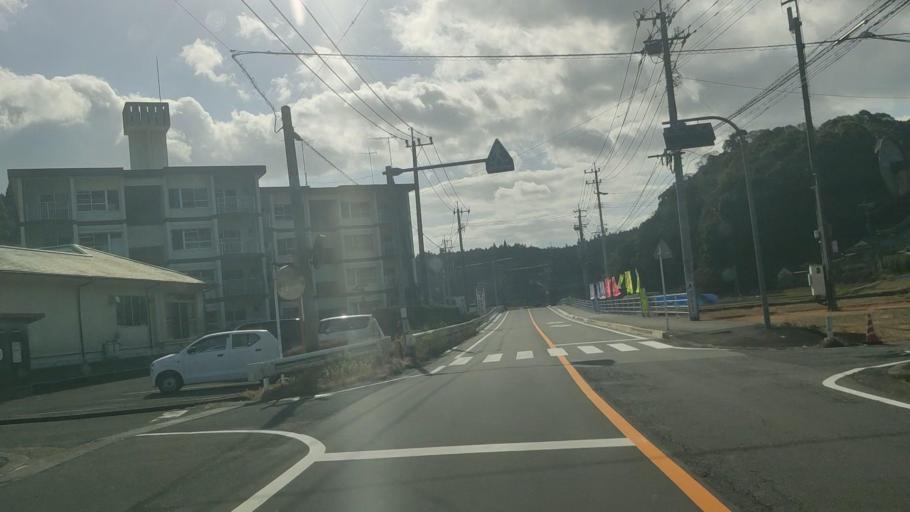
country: JP
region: Kagoshima
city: Okuchi-shinohara
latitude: 31.9427
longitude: 130.7103
